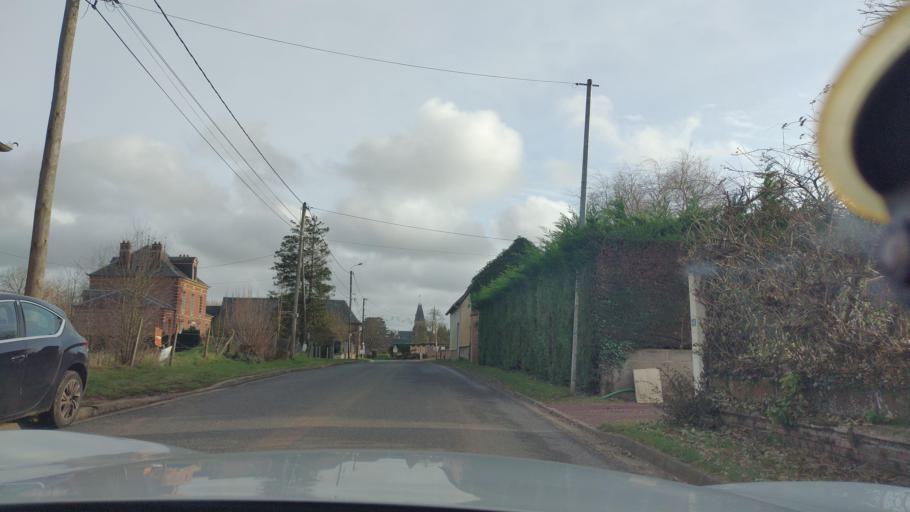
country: FR
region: Picardie
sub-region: Departement de la Somme
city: Beaucamps-le-Vieux
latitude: 49.8711
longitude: 1.8280
